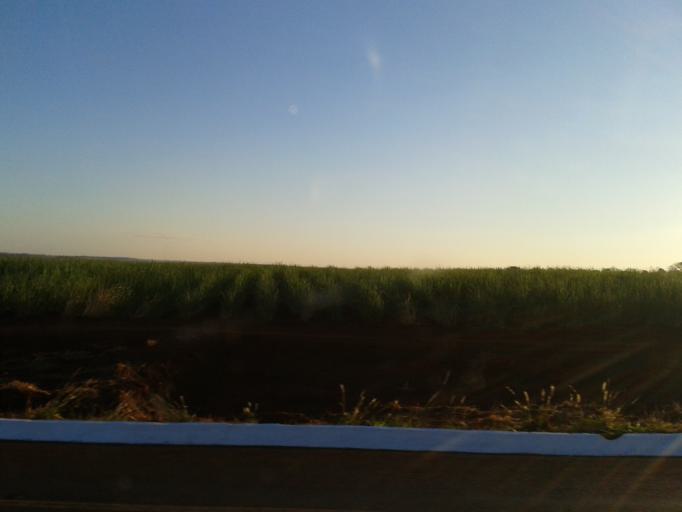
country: BR
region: Minas Gerais
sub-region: Centralina
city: Centralina
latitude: -18.7122
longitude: -49.2791
